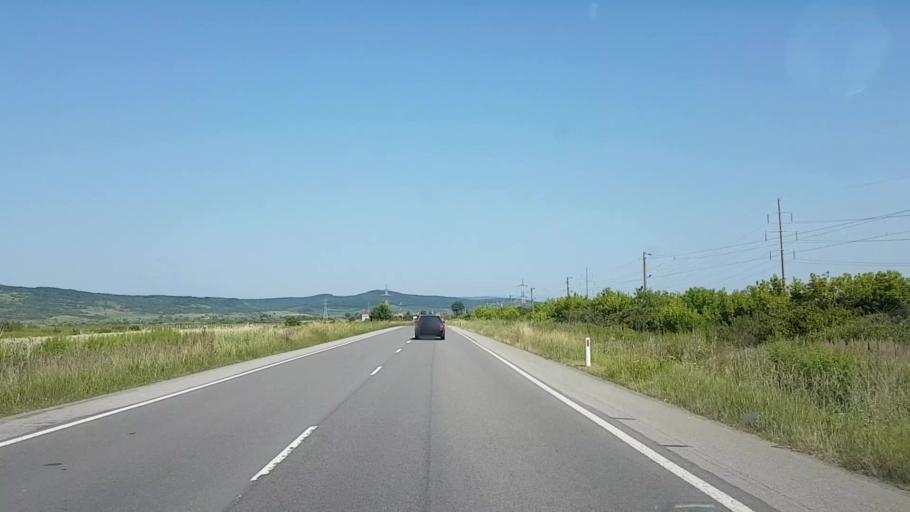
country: RO
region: Bistrita-Nasaud
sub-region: Comuna Sintereag
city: Cociu
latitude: 47.1821
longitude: 24.2458
